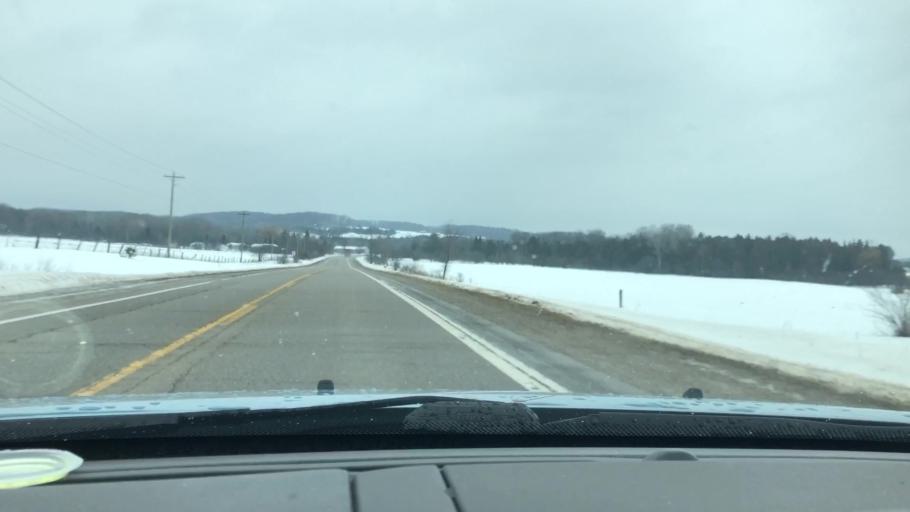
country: US
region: Michigan
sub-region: Charlevoix County
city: East Jordan
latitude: 45.1259
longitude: -85.1346
